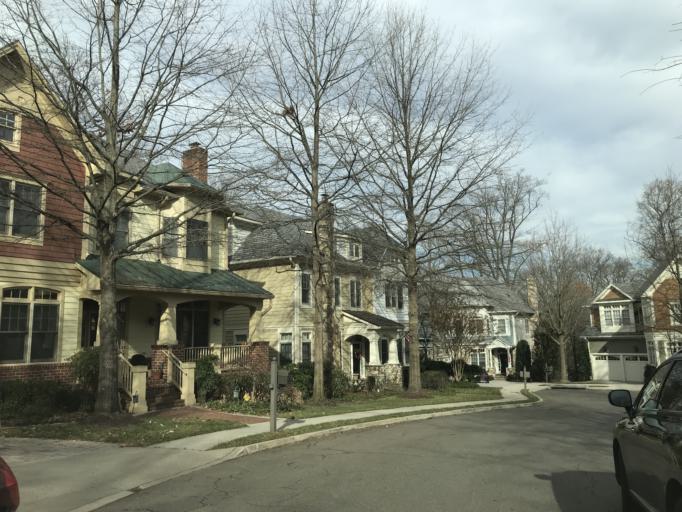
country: US
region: Virginia
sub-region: Arlington County
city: Arlington
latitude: 38.9005
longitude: -77.0986
